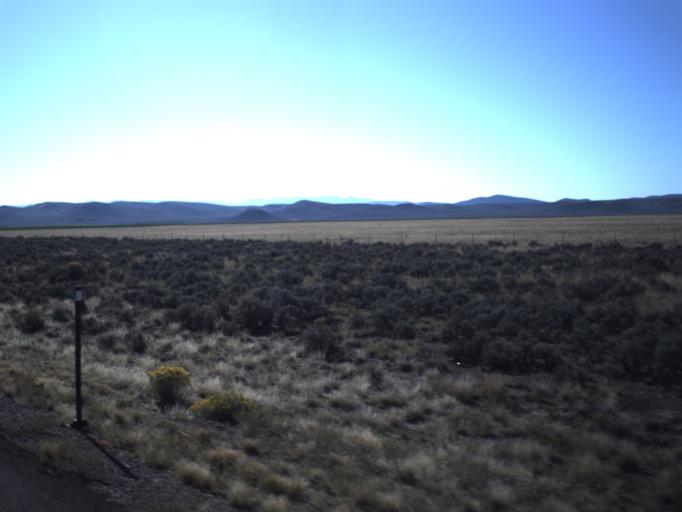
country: US
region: Utah
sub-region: Washington County
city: Enterprise
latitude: 37.7654
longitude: -113.8146
